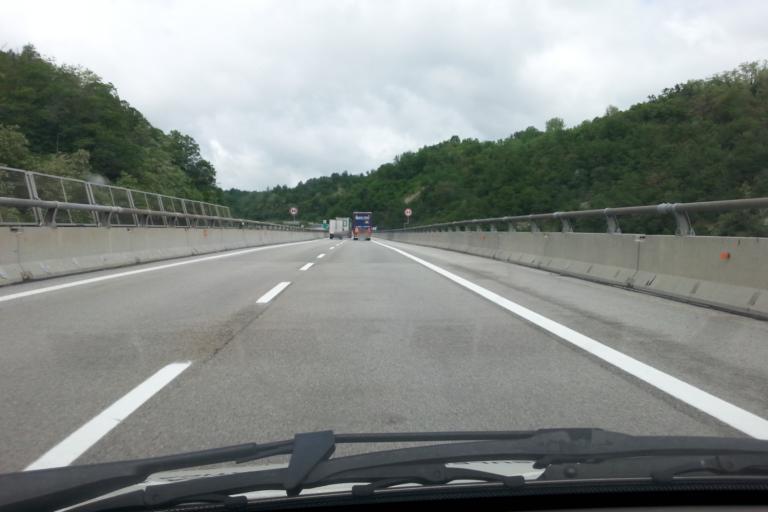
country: IT
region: Liguria
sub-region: Provincia di Savona
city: Valzemola
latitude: 44.3583
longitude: 8.1689
